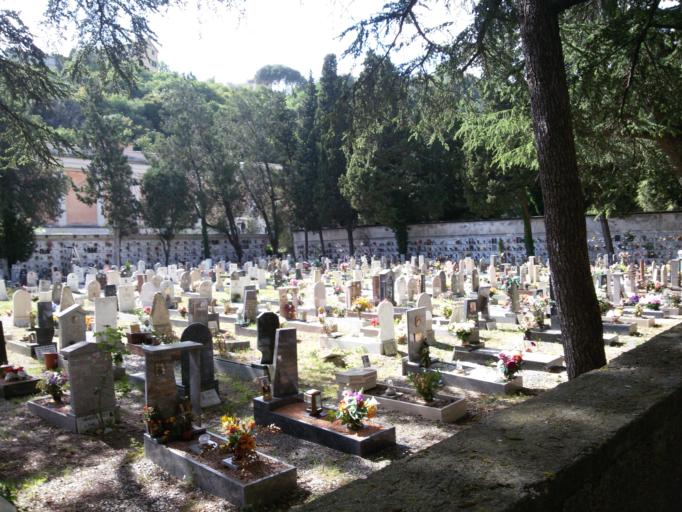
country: IT
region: Liguria
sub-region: Provincia di Genova
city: Genoa
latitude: 44.4315
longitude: 8.9482
